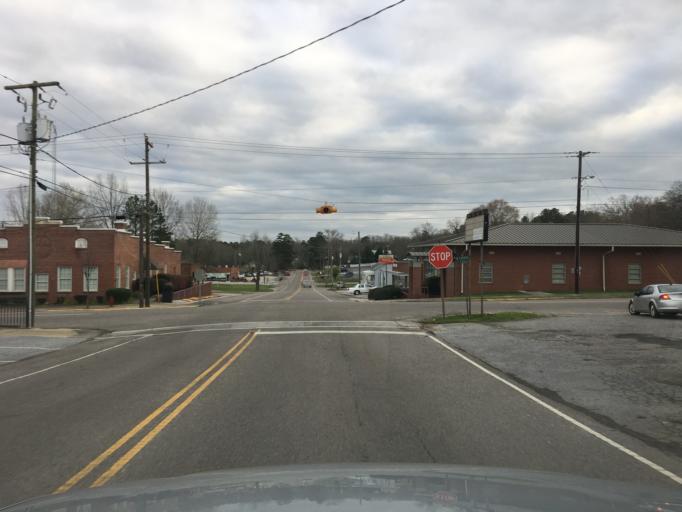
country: US
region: South Carolina
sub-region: Saluda County
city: Saluda
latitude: 34.0019
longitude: -81.7735
